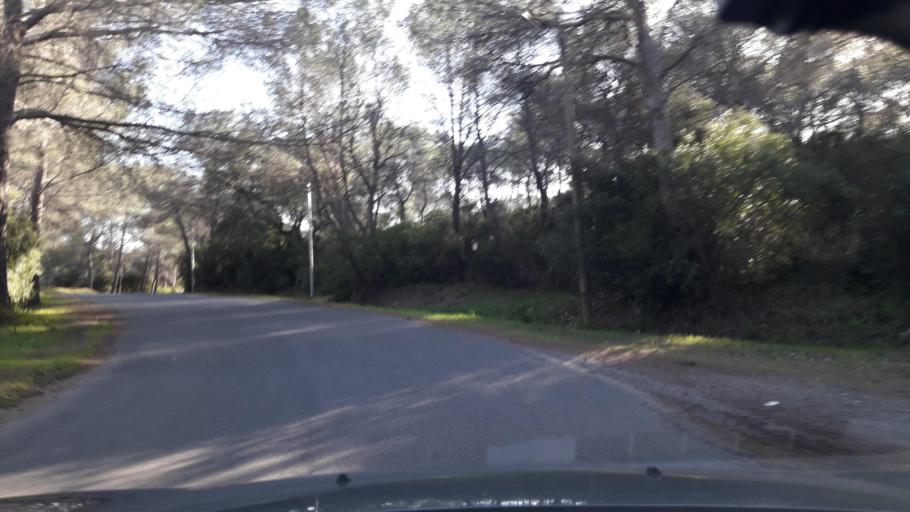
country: FR
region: Provence-Alpes-Cote d'Azur
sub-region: Departement du Var
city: Saint-Raphael
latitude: 43.4211
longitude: 6.8232
